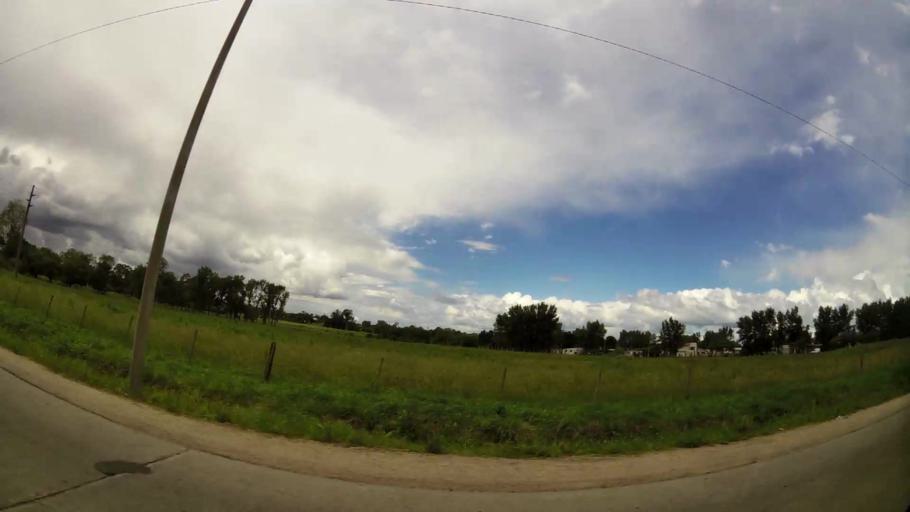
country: UY
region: Canelones
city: La Paz
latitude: -34.8012
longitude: -56.1566
